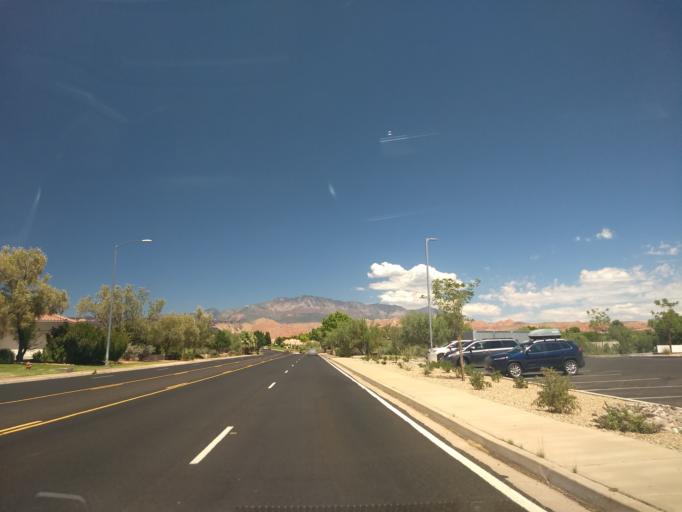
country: US
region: Utah
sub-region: Washington County
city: Washington
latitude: 37.1331
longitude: -113.5266
